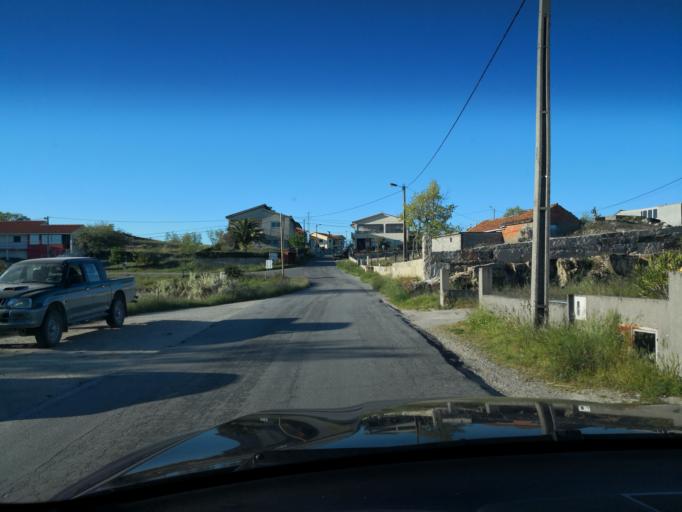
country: PT
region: Vila Real
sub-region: Vila Real
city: Vila Real
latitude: 41.3550
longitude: -7.6627
